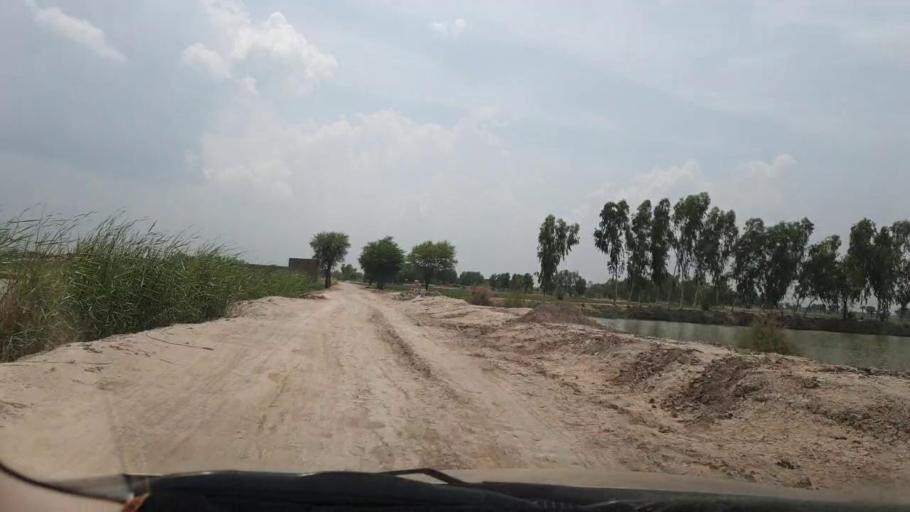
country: PK
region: Sindh
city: Larkana
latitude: 27.6190
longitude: 68.1551
